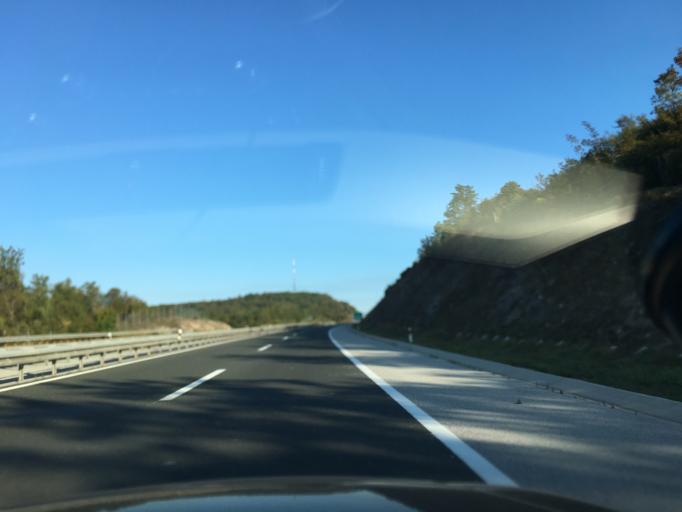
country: HR
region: Licko-Senjska
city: Gospic
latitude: 44.7374
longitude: 15.3796
